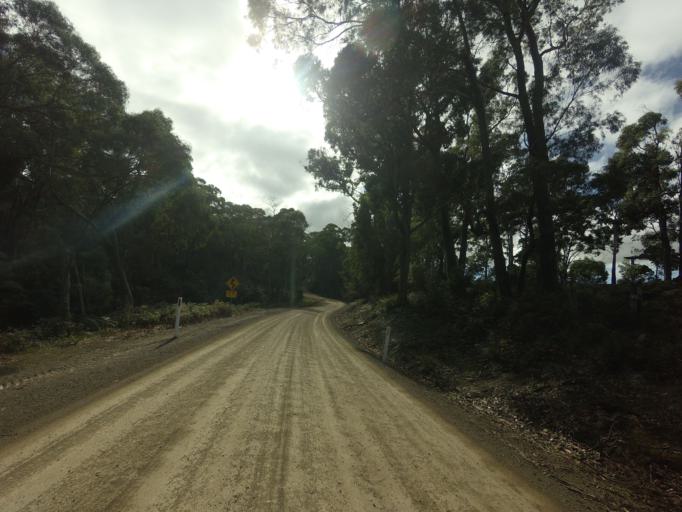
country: AU
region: Tasmania
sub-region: Clarence
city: Sandford
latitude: -43.0895
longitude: 147.7151
